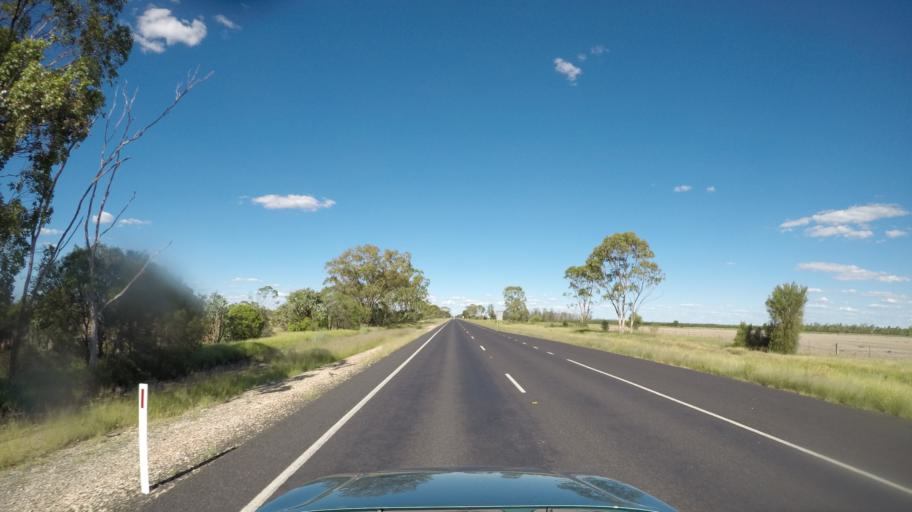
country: AU
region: Queensland
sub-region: Goondiwindi
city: Goondiwindi
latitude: -28.1752
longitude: 150.4848
